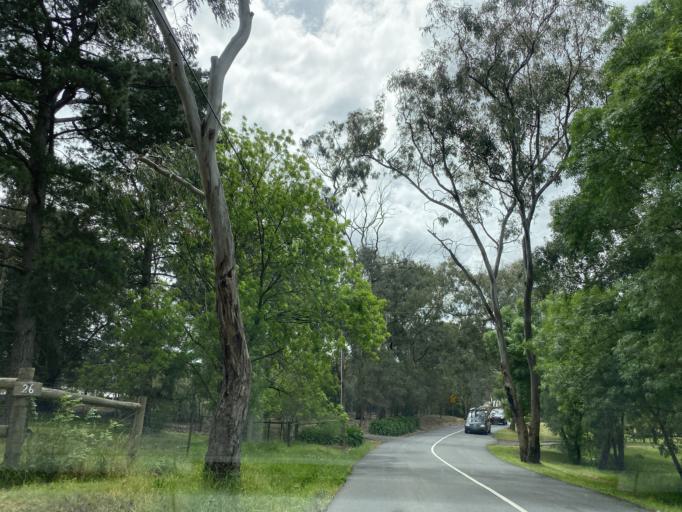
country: AU
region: Victoria
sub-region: Banyule
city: Lower Plenty
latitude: -37.7398
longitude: 145.1089
